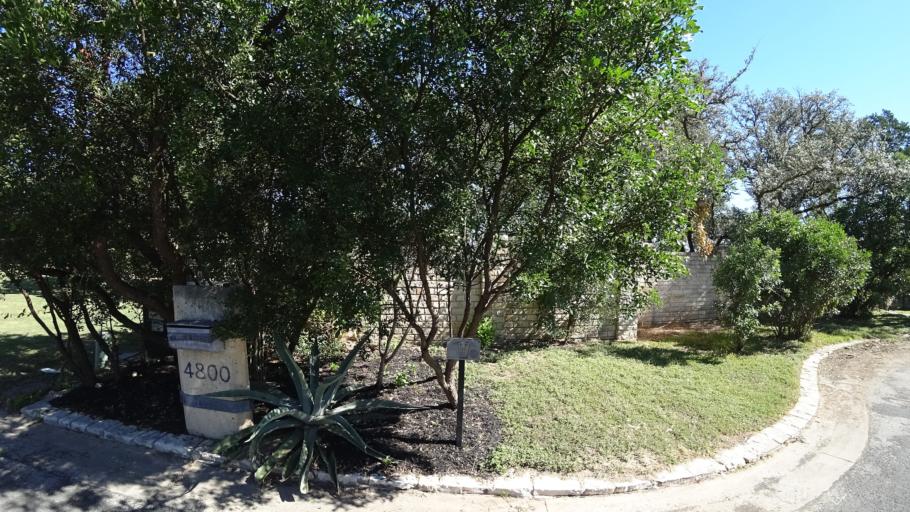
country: US
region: Texas
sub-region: Travis County
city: West Lake Hills
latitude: 30.3209
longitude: -97.7913
